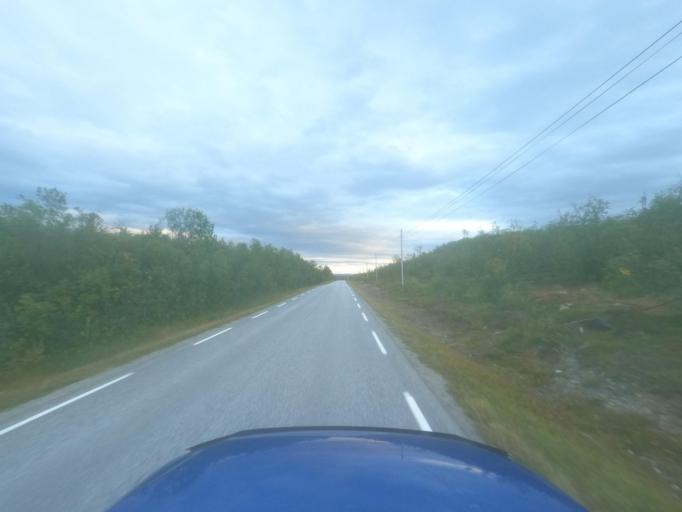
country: NO
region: Finnmark Fylke
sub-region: Porsanger
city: Lakselv
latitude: 70.1991
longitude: 24.9135
